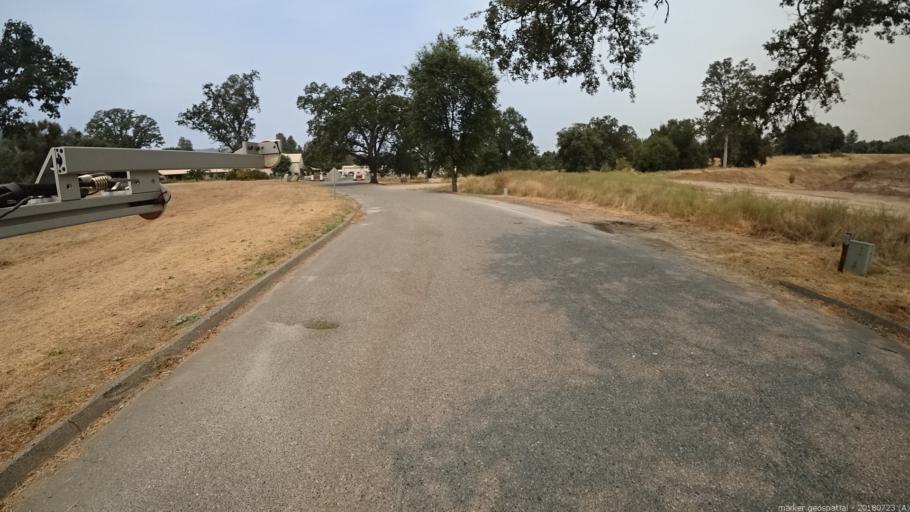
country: US
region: California
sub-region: Madera County
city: Oakhurst
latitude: 37.3401
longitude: -119.6691
